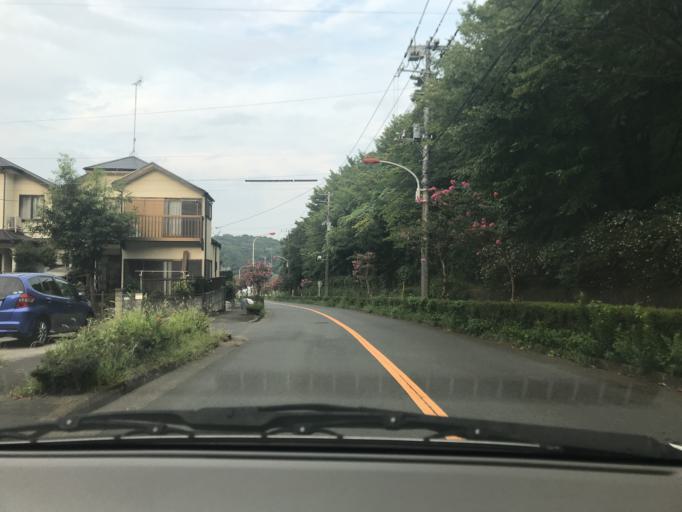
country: JP
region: Kanagawa
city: Fujisawa
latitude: 35.3632
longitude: 139.4515
